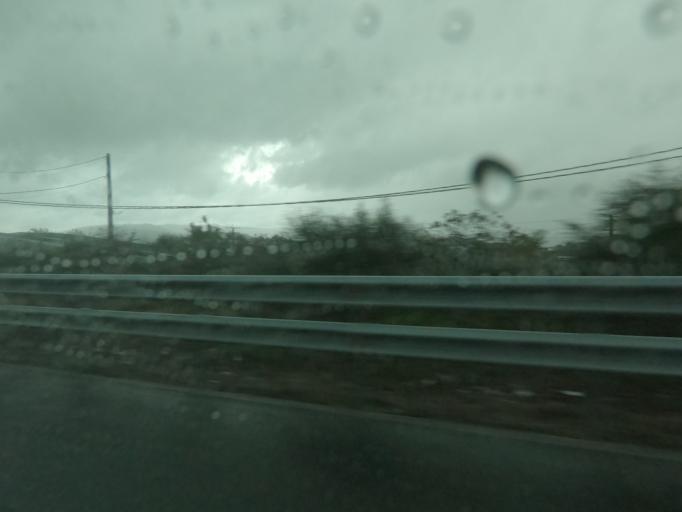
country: ES
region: Galicia
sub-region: Provincia de Pontevedra
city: Marin
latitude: 42.3476
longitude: -8.6467
